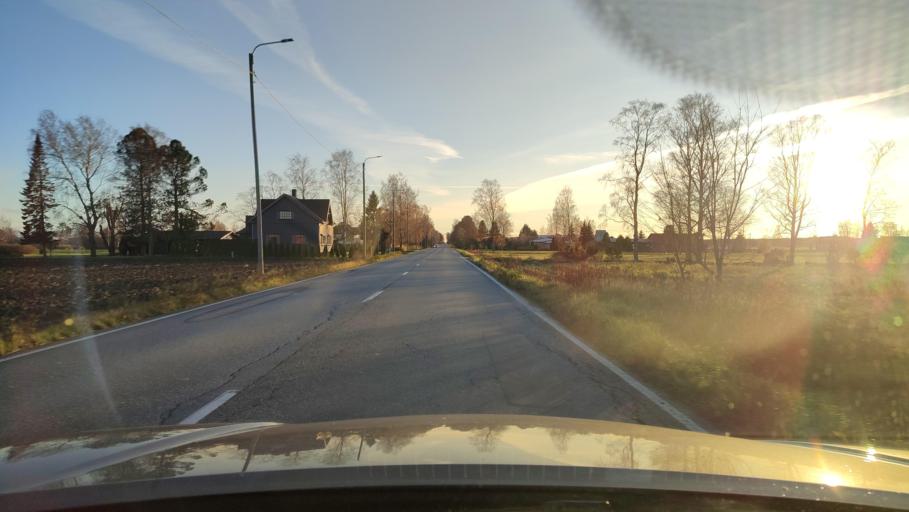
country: FI
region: Ostrobothnia
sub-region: Sydosterbotten
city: Naerpes
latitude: 62.5993
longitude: 21.4534
